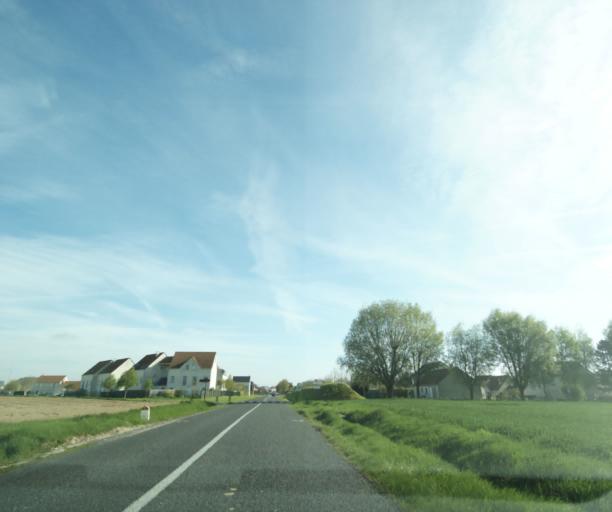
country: FR
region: Ile-de-France
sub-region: Departement de Seine-et-Marne
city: Nangis
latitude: 48.5517
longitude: 3.0017
